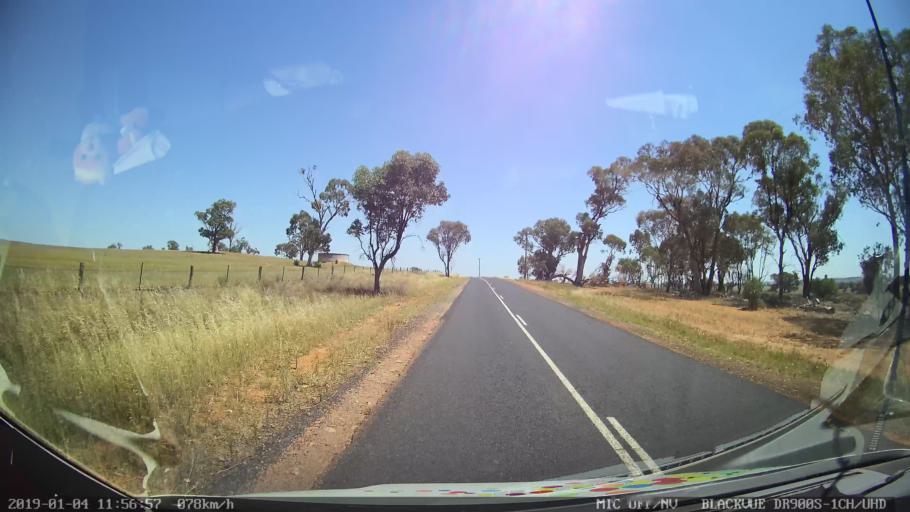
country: AU
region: New South Wales
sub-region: Cabonne
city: Molong
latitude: -32.8401
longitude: 148.7109
